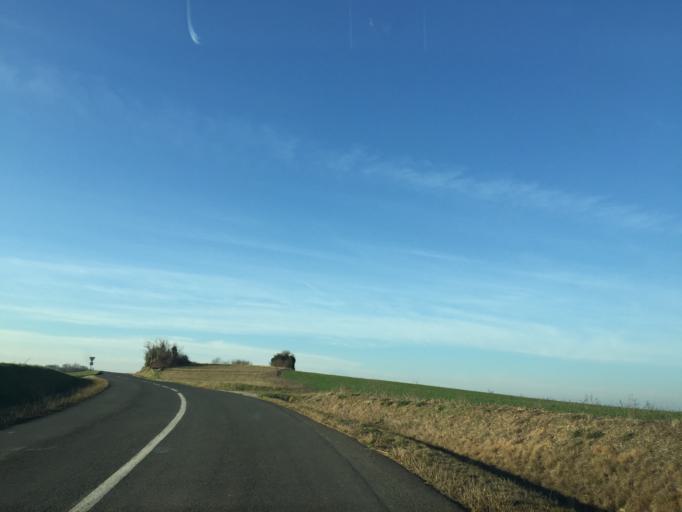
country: FR
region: Aquitaine
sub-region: Departement de la Dordogne
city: Riberac
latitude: 45.2320
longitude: 0.2632
